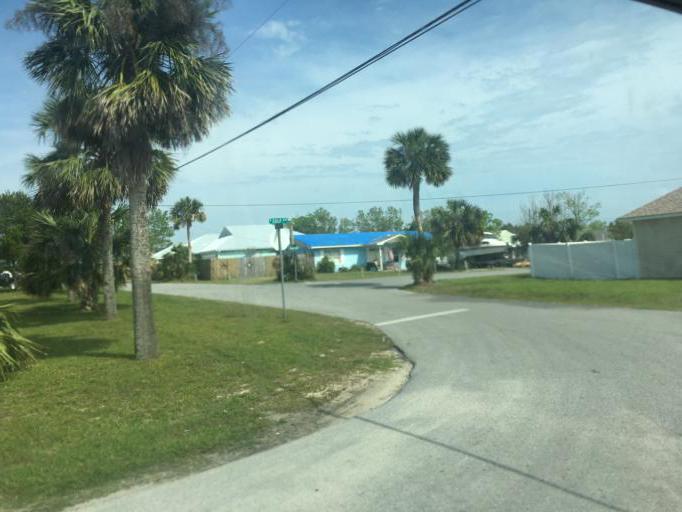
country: US
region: Florida
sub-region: Bay County
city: Panama City Beach
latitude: 30.2079
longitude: -85.8571
